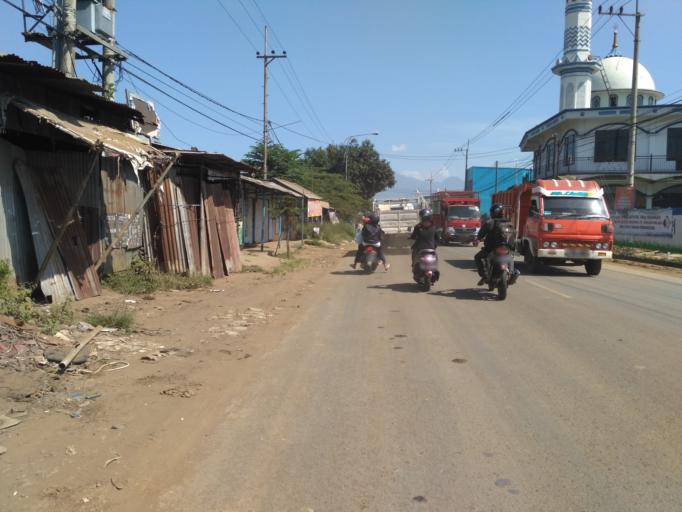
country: ID
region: East Java
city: Tamiajeng
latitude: -7.9532
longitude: 112.6949
